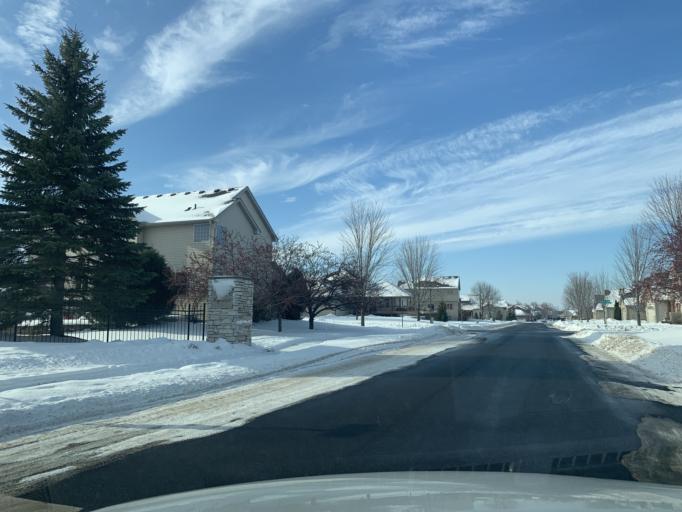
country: US
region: Minnesota
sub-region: Wright County
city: Albertville
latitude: 45.2210
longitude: -93.6442
